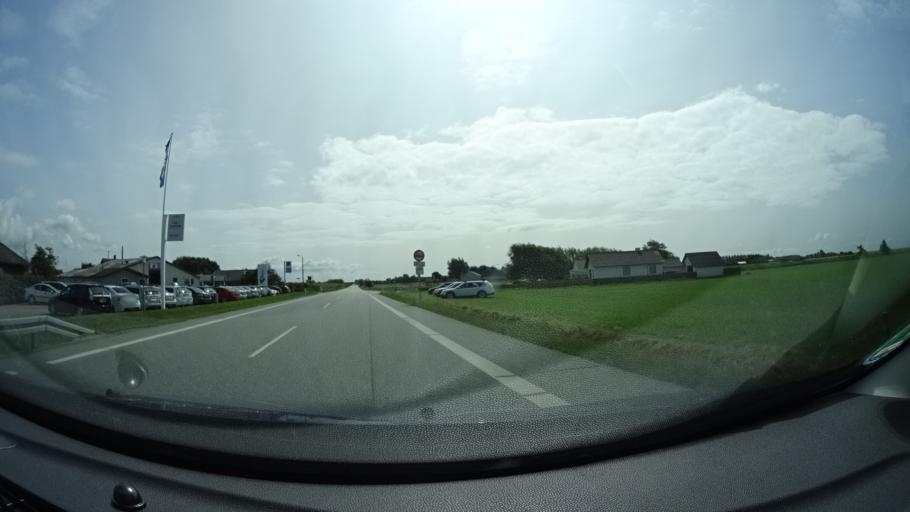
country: DE
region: Schleswig-Holstein
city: Rodenas
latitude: 54.9744
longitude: 8.6992
